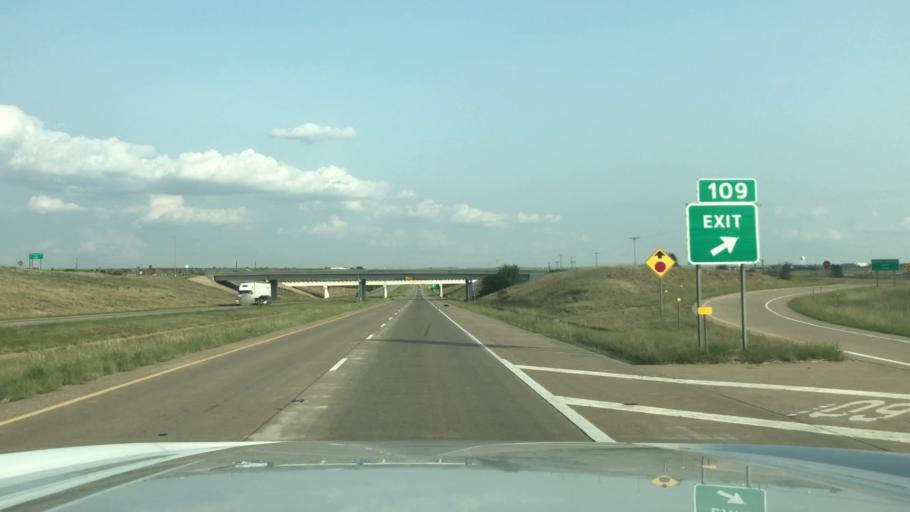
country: US
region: Texas
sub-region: Randall County
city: Canyon
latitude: 35.0156
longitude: -101.9127
